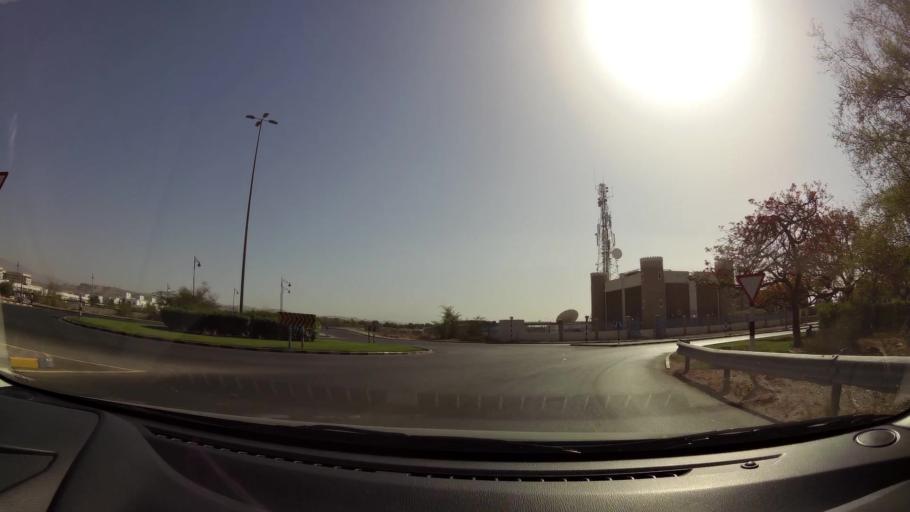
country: OM
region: Muhafazat Masqat
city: Bawshar
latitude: 23.5828
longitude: 58.2924
